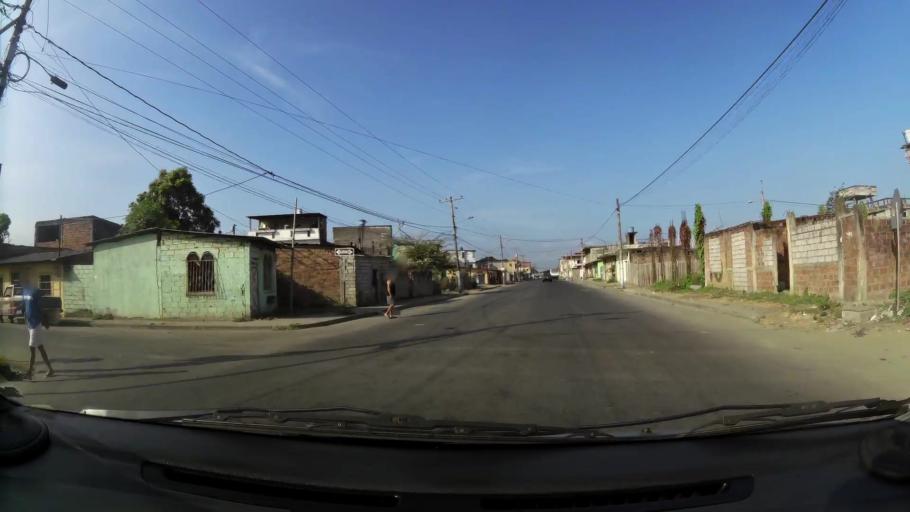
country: EC
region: Guayas
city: Eloy Alfaro
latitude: -2.1838
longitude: -79.8461
